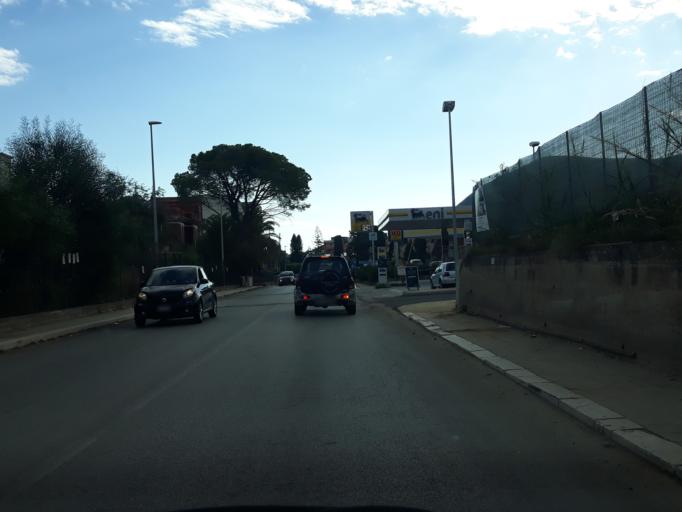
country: IT
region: Sicily
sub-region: Palermo
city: Cefalu
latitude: 38.0307
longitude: 13.9989
